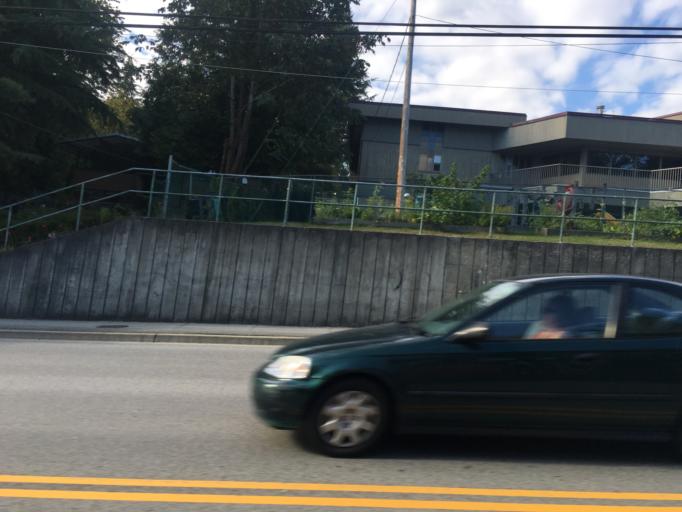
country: CA
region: British Columbia
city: Port Moody
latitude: 49.2489
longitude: -122.8554
